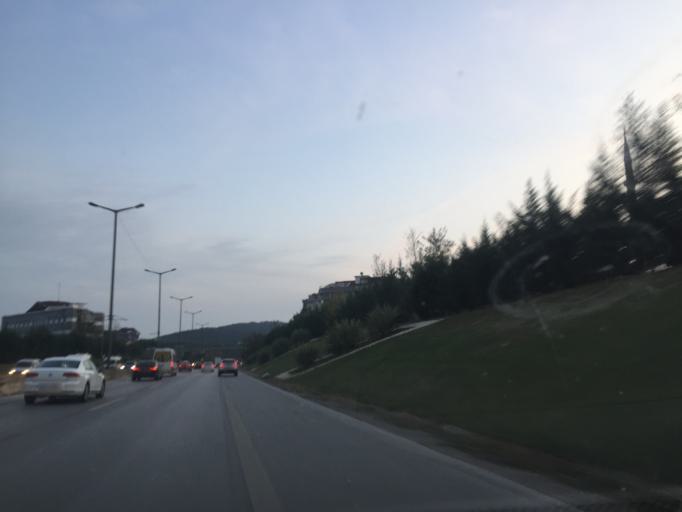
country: TR
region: Istanbul
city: Samandira
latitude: 40.9630
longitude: 29.2203
